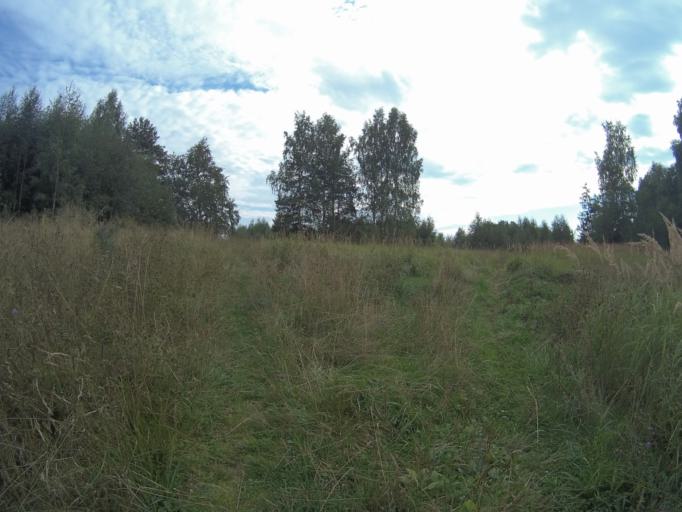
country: RU
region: Vladimir
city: Raduzhnyy
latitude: 56.0069
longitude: 40.3213
